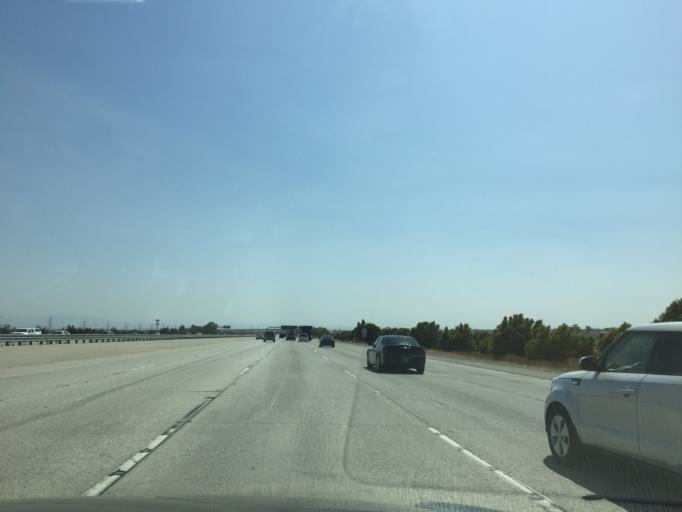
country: US
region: California
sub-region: San Bernardino County
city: Fontana
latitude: 34.1484
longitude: -117.4816
